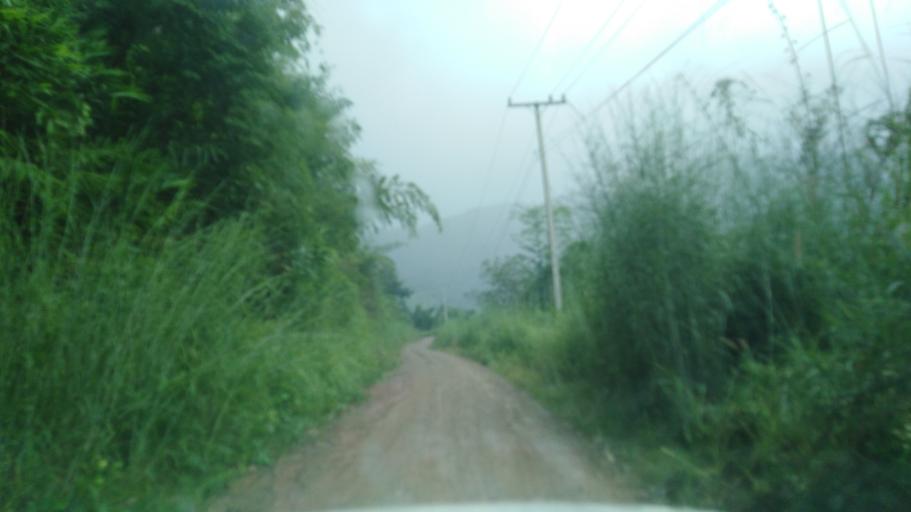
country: TH
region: Phayao
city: Phu Sang
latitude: 19.7560
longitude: 100.6675
